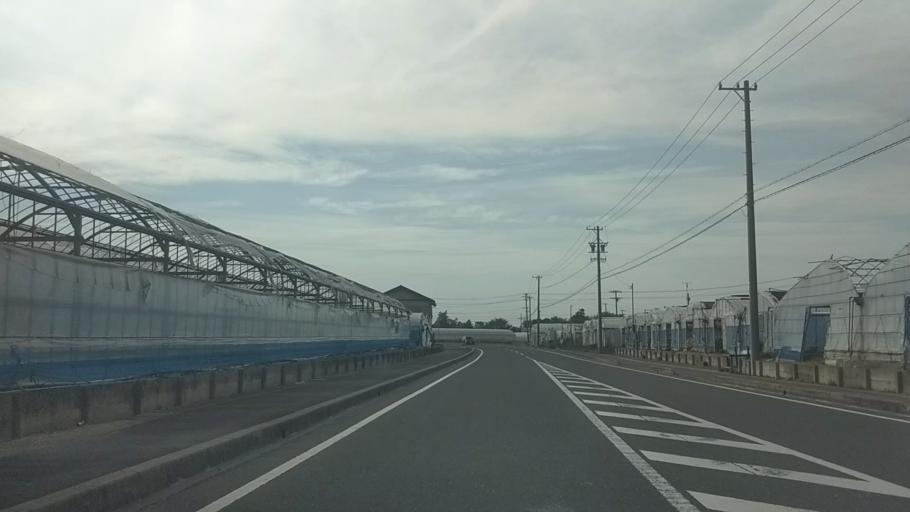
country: JP
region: Shizuoka
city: Hamamatsu
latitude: 34.7238
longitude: 137.6501
